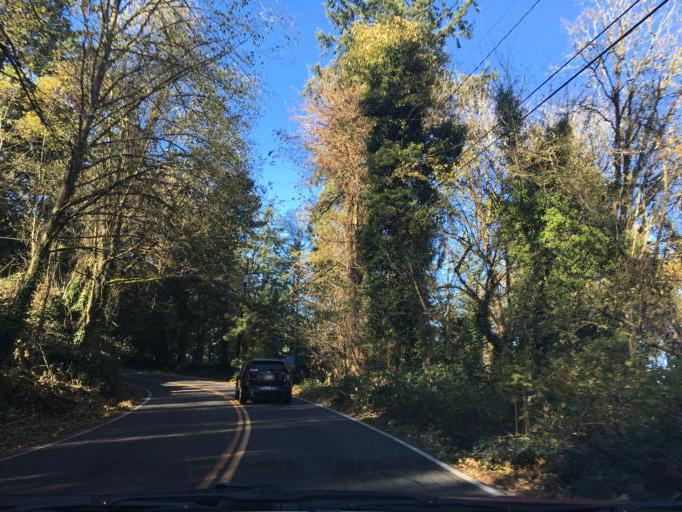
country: US
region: Oregon
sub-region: Washington County
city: Cedar Mill
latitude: 45.5901
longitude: -122.7823
